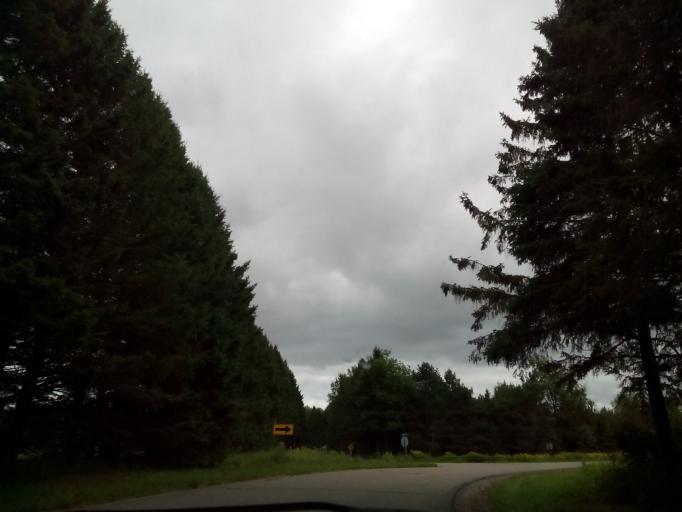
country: US
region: Wisconsin
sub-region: Menominee County
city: Legend Lake
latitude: 45.3268
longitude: -88.5289
